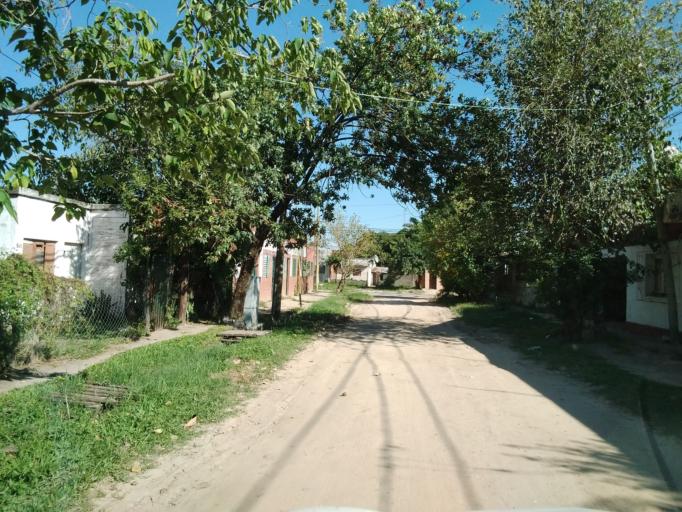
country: AR
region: Corrientes
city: Corrientes
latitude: -27.4811
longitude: -58.8056
